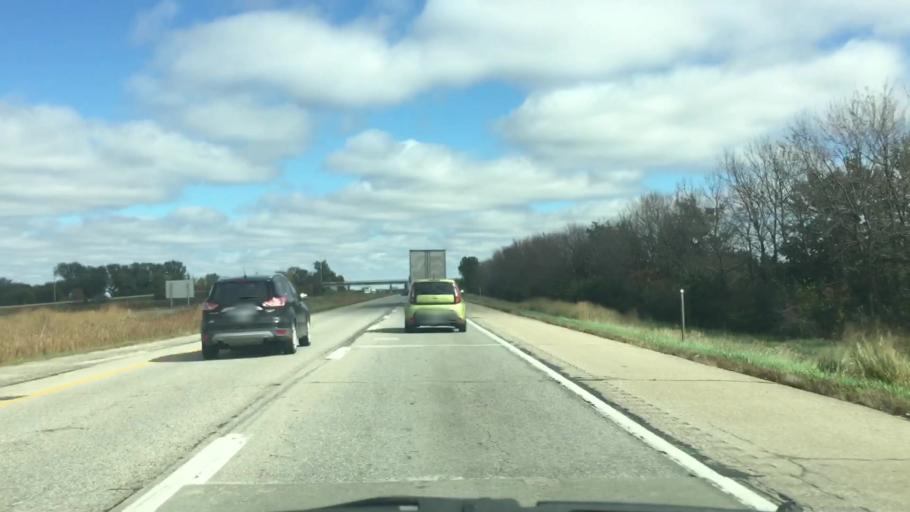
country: US
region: Iowa
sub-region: Jasper County
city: Newton
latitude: 41.6853
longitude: -92.8866
